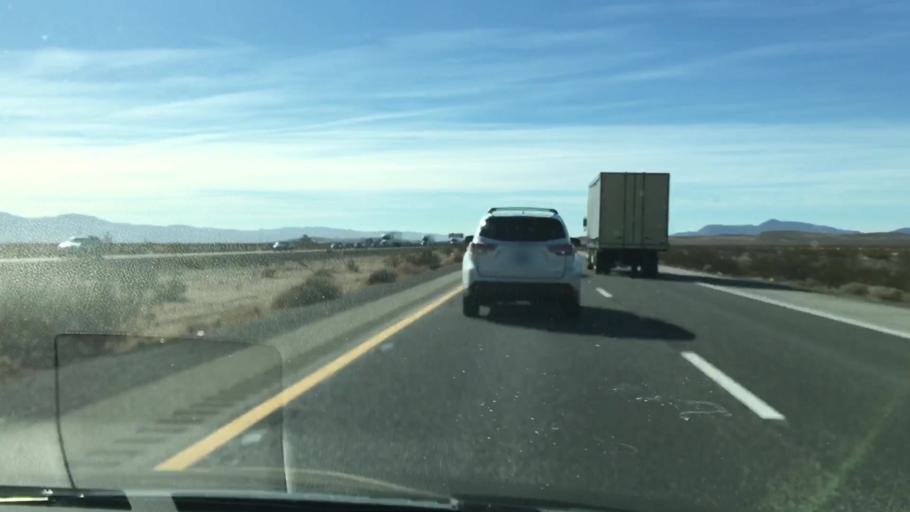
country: US
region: California
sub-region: San Bernardino County
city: Fort Irwin
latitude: 34.9830
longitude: -116.6008
